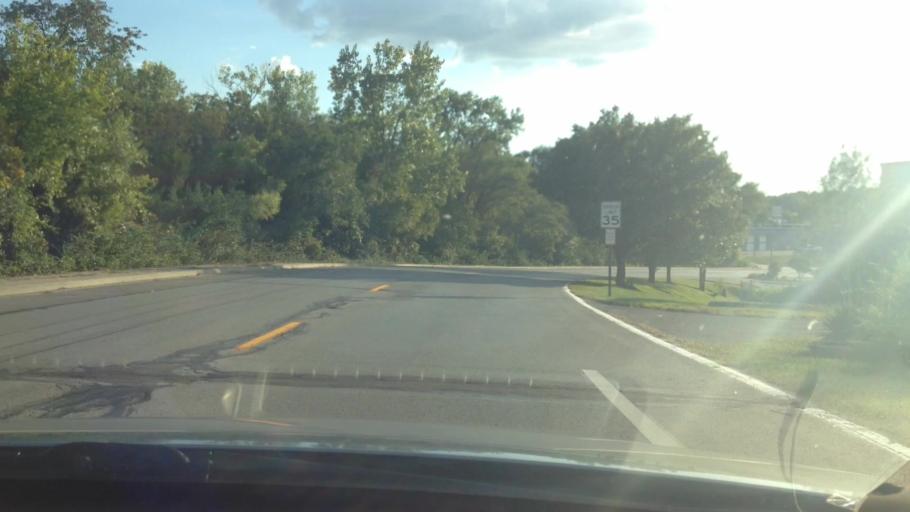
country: US
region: Missouri
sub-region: Jackson County
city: Grandview
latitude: 38.8975
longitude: -94.5215
